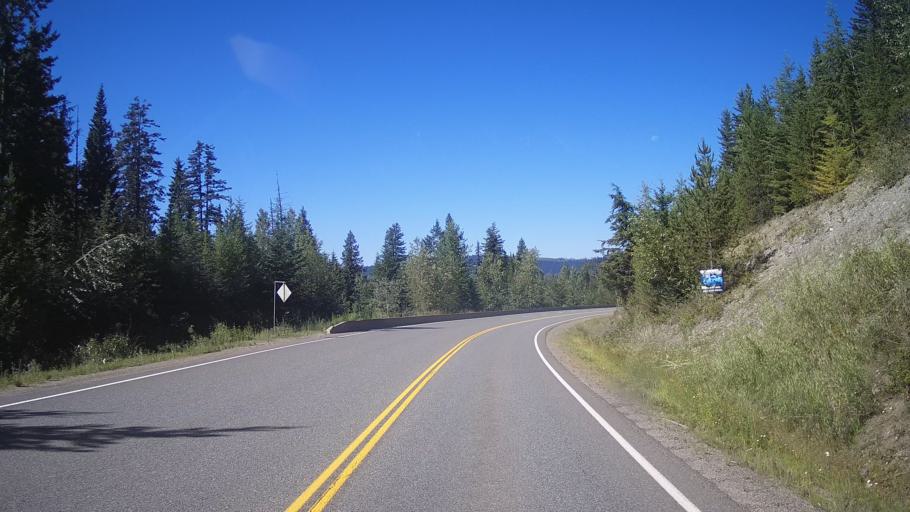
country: CA
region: British Columbia
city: Kamloops
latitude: 51.4768
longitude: -120.4749
